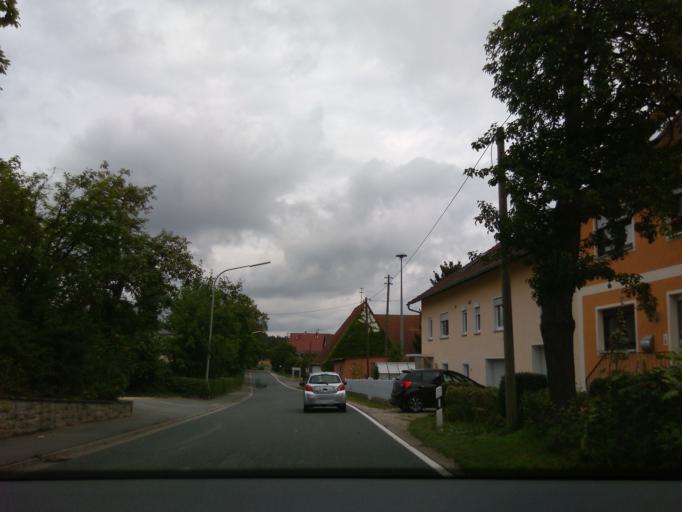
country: DE
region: Bavaria
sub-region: Regierungsbezirk Mittelfranken
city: Weisendorf
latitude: 49.6563
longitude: 10.8095
